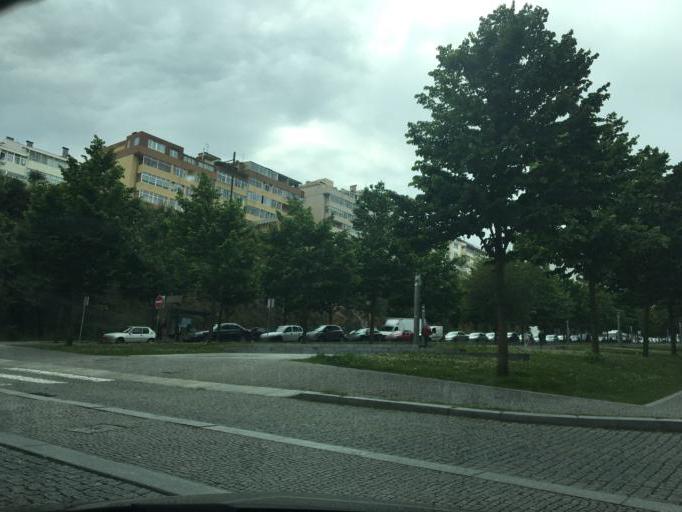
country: PT
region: Porto
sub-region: Porto
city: Porto
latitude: 41.1630
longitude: -8.5855
